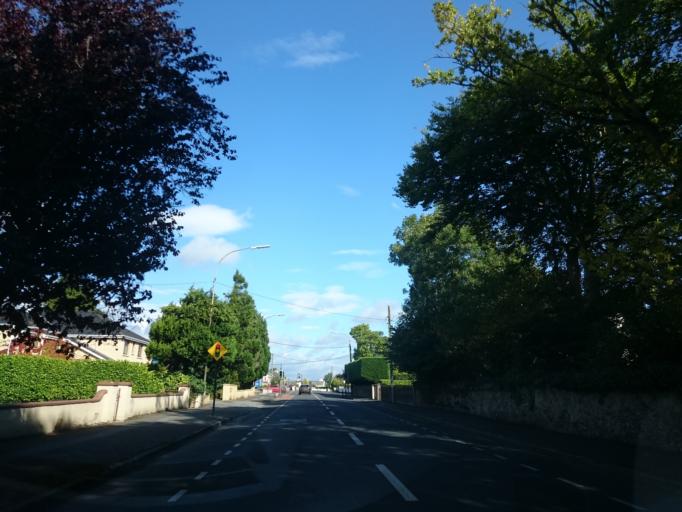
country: IE
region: Leinster
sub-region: Kilkenny
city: Kilkenny
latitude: 52.6657
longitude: -7.2520
